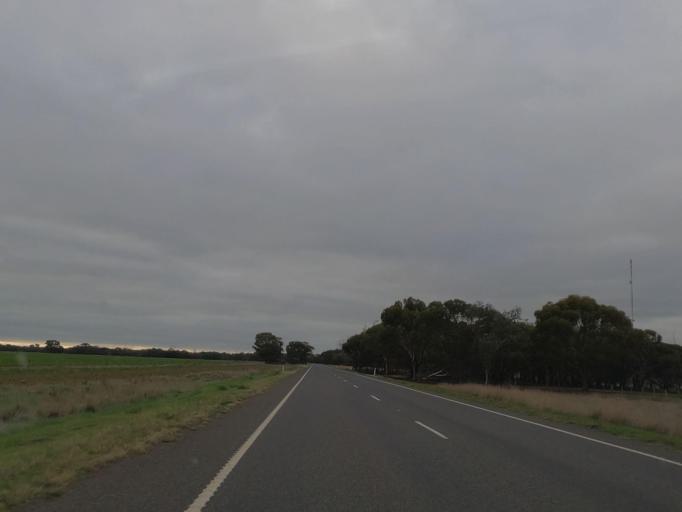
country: AU
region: Victoria
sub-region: Greater Bendigo
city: Long Gully
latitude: -36.0685
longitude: 143.9447
